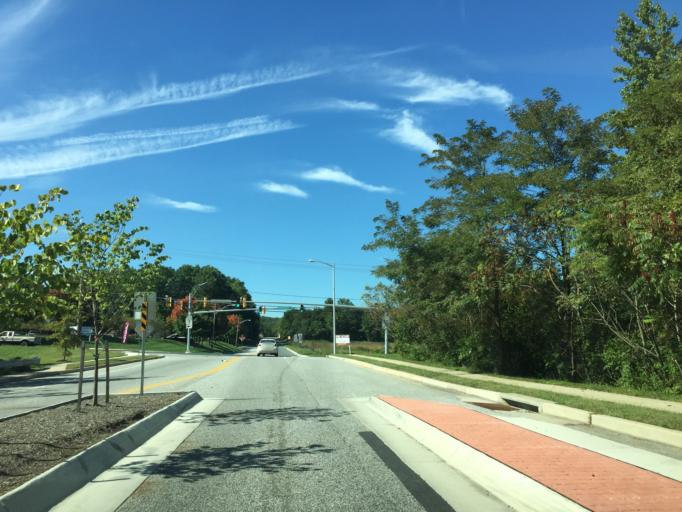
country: US
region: Maryland
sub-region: Baltimore County
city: White Marsh
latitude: 39.4069
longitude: -76.4119
